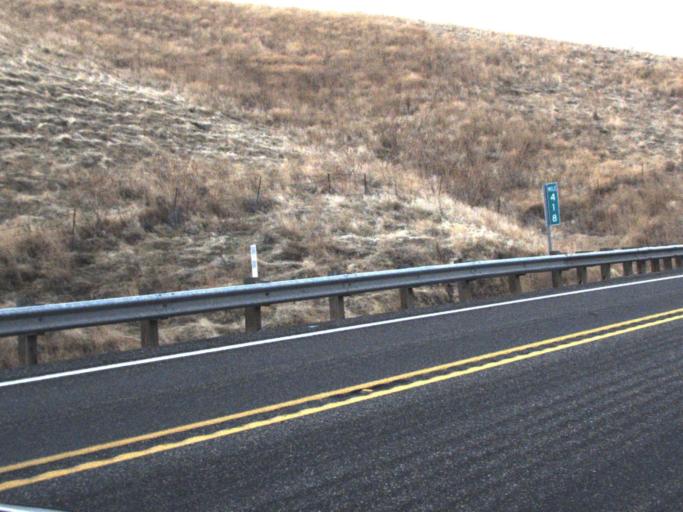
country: US
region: Washington
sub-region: Asotin County
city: Clarkston Heights-Vineland
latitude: 46.4332
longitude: -117.3362
